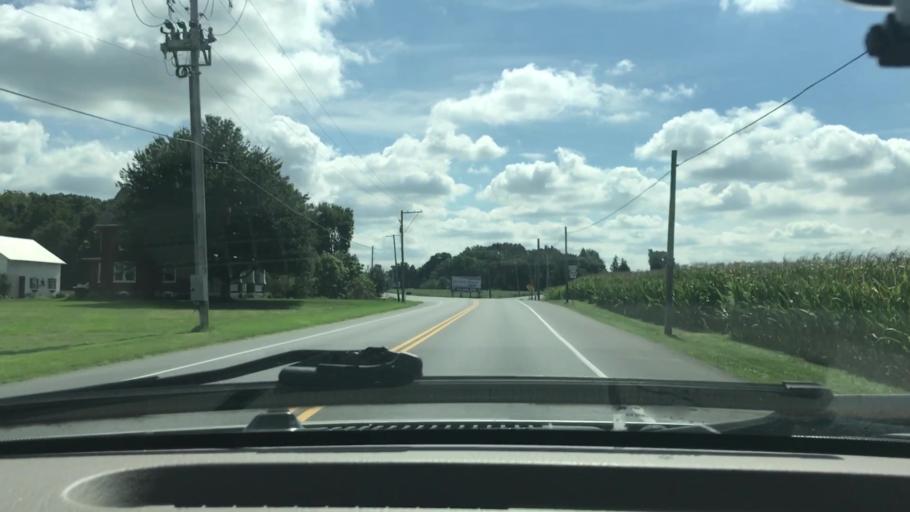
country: US
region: Pennsylvania
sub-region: Lancaster County
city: East Petersburg
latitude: 40.1271
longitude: -76.3793
